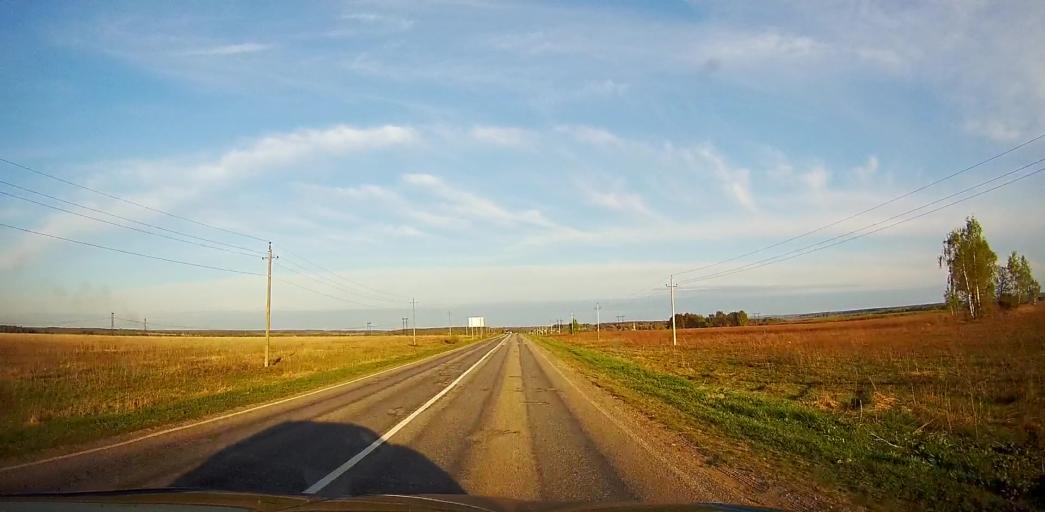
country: RU
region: Moskovskaya
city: Meshcherino
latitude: 55.2678
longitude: 38.2479
